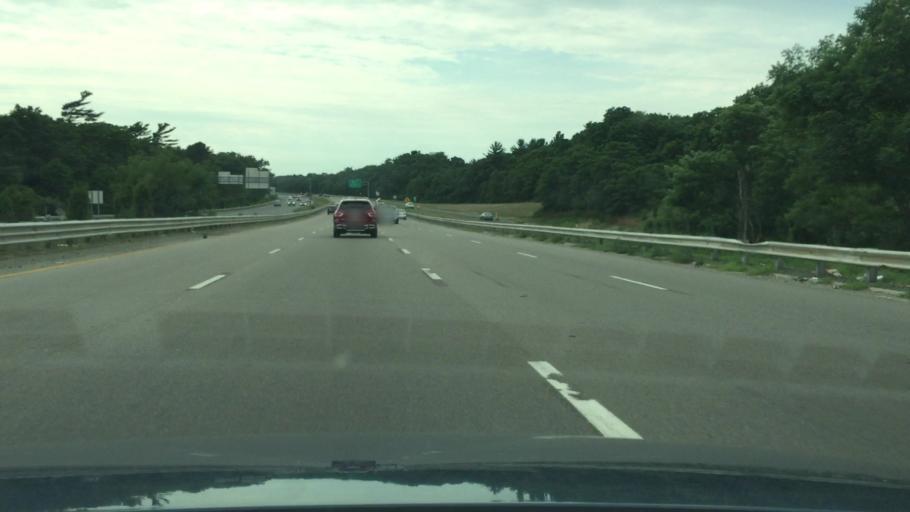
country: US
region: Massachusetts
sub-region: Plymouth County
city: North Plymouth
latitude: 41.9553
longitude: -70.6830
